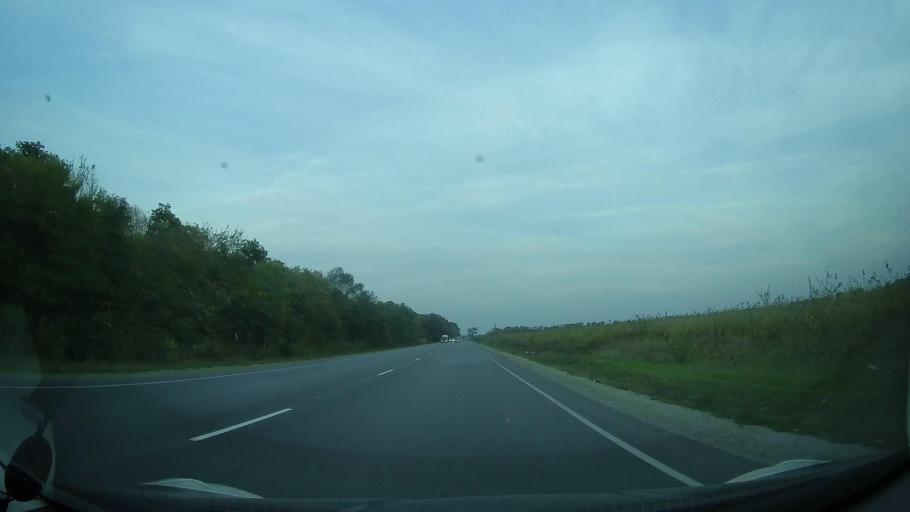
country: RU
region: Rostov
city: Ol'ginskaya
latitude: 47.1311
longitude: 39.9444
